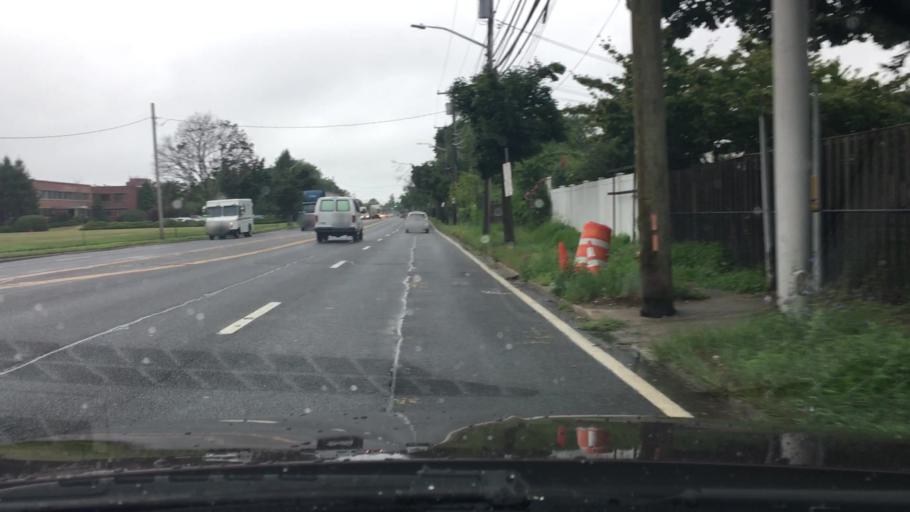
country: US
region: New York
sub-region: Nassau County
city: Hicksville
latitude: 40.7671
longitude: -73.5095
